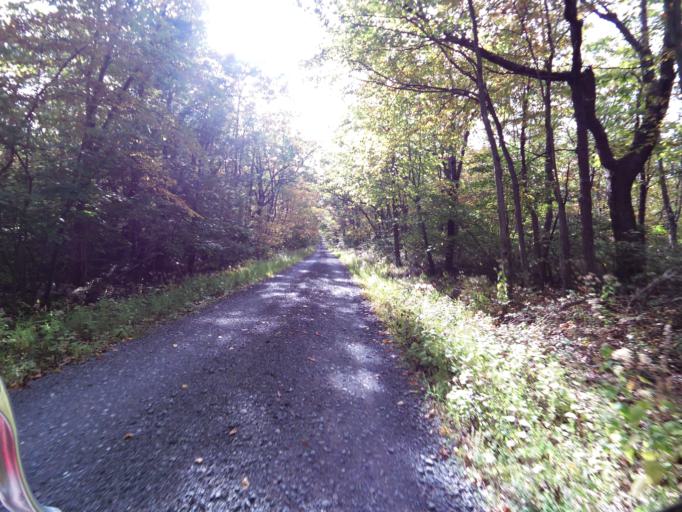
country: US
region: Pennsylvania
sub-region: Lycoming County
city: Jersey Shore
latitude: 41.1079
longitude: -77.1572
